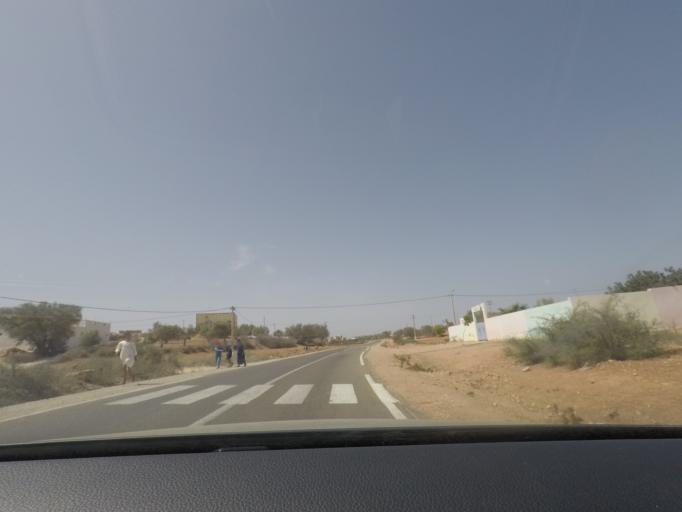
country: MA
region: Marrakech-Tensift-Al Haouz
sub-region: Essaouira
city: Tamanar
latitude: 31.0266
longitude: -9.6703
